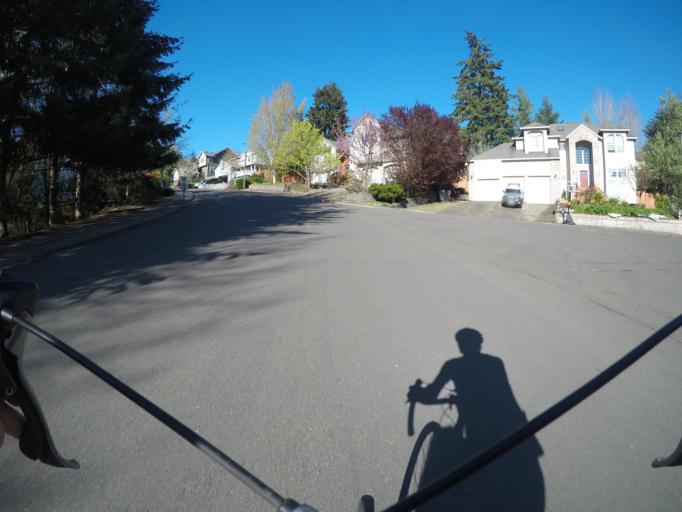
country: US
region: Oregon
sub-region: Washington County
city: King City
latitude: 45.4063
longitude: -122.8273
